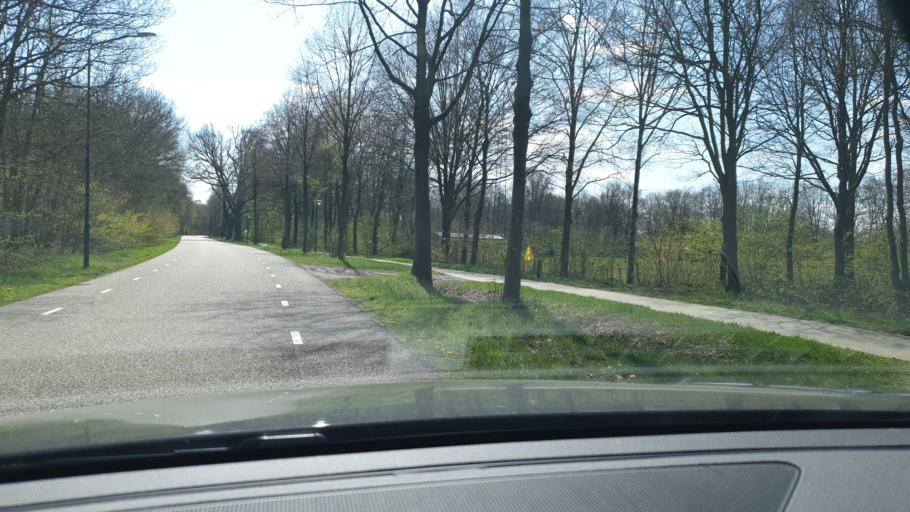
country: NL
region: North Brabant
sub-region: Gemeente Bladel en Netersel
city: Bladel
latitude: 51.3820
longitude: 5.2565
